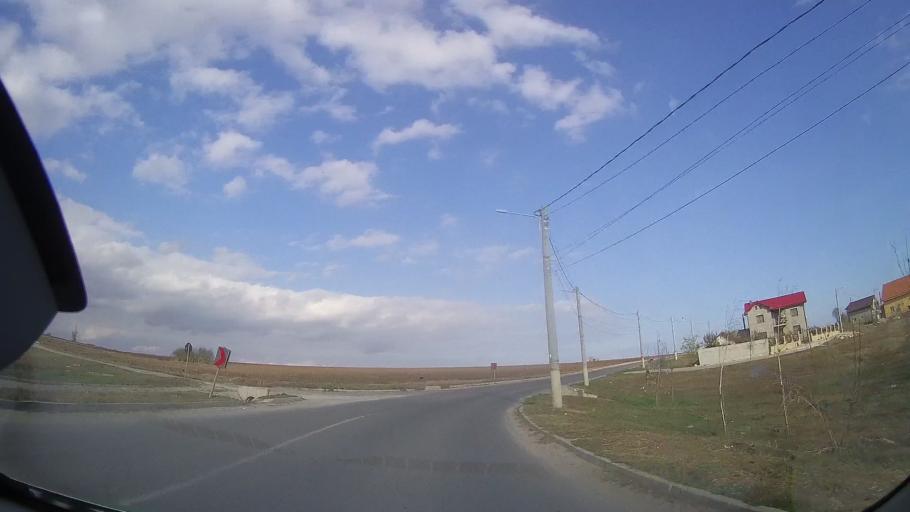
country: RO
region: Constanta
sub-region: Comuna Douazeci si Trei August
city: Dulcesti
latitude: 43.9109
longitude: 28.5503
